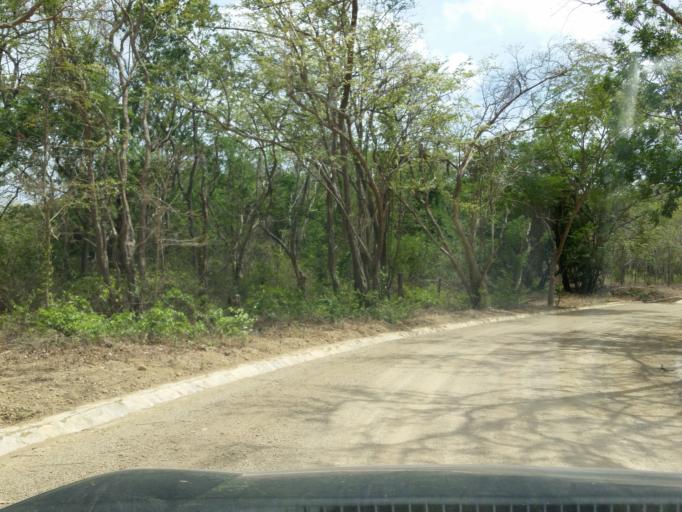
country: NI
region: Rivas
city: Tola
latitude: 11.4406
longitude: -86.0821
